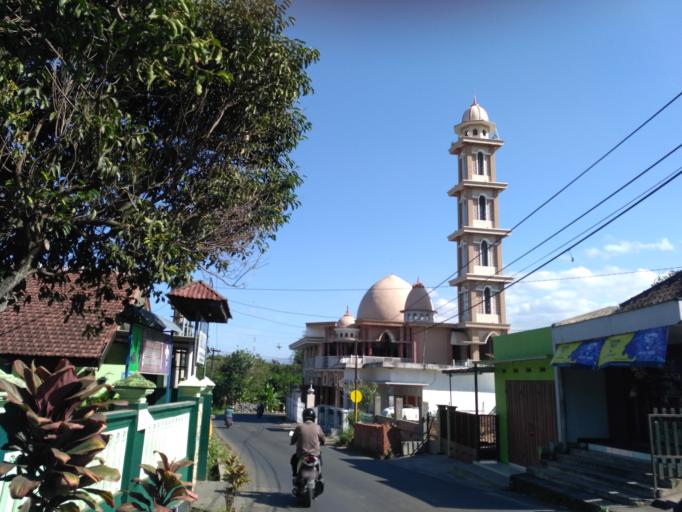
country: ID
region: East Java
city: Singosari
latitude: -7.9196
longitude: 112.6654
